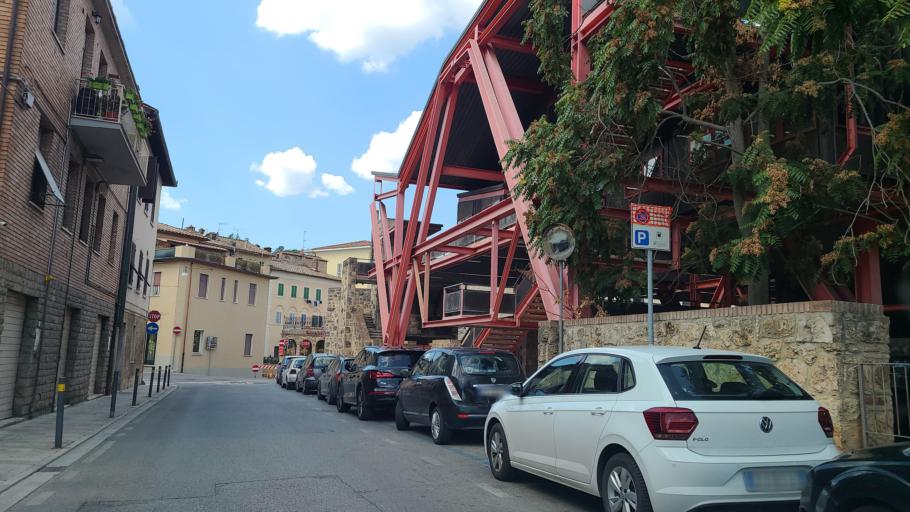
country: IT
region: Tuscany
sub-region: Provincia di Siena
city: Colle di Val d'Elsa
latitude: 43.4232
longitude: 11.1272
